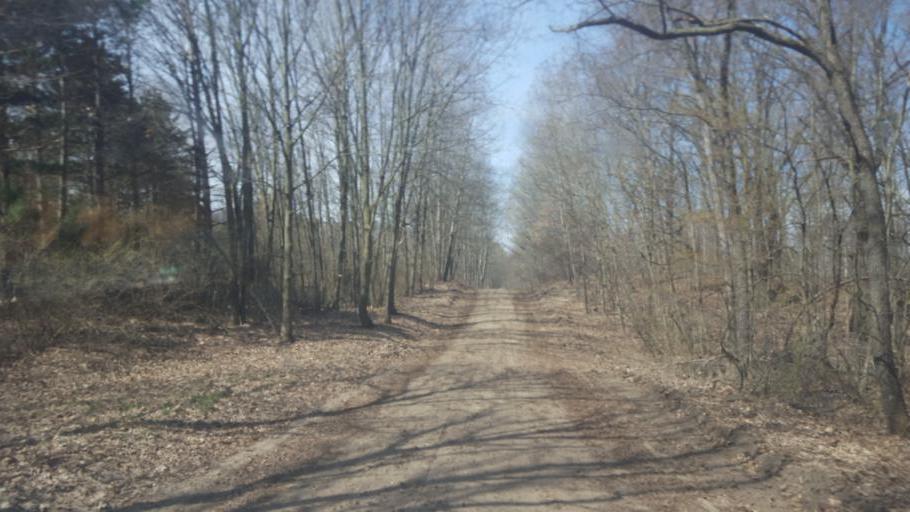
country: US
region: Michigan
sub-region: Montcalm County
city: Edmore
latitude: 43.4662
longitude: -84.9278
